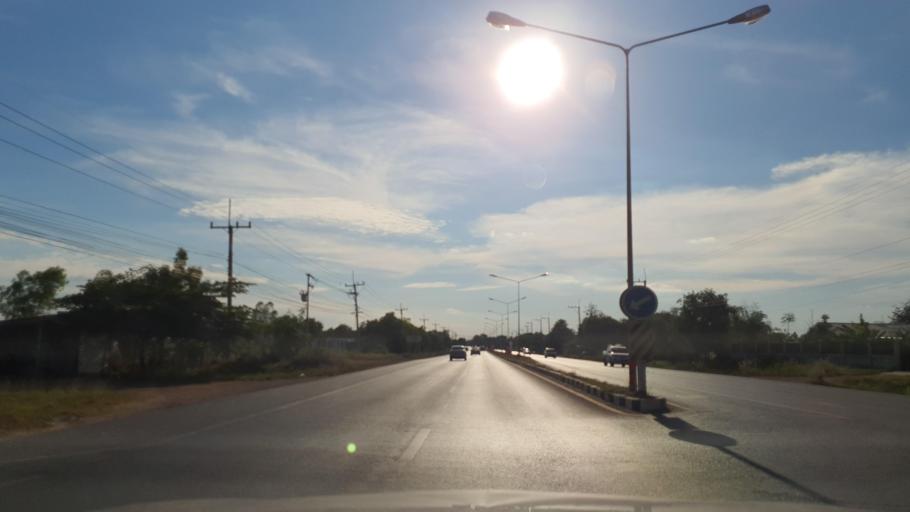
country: TH
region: Maha Sarakham
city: Kantharawichai
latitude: 16.3525
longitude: 103.3288
